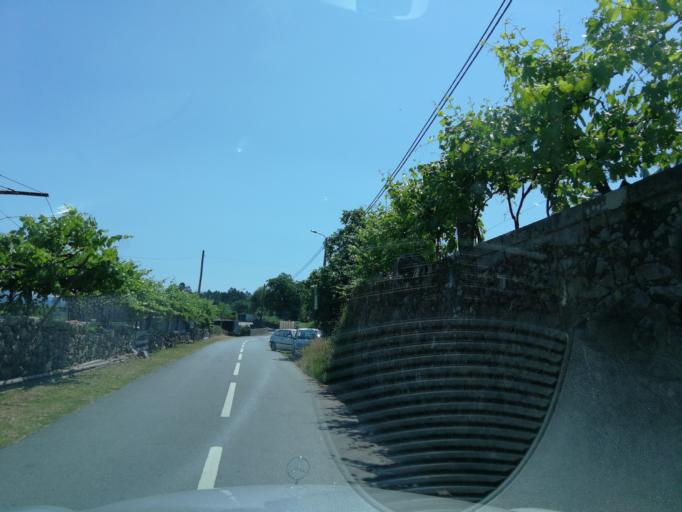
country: PT
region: Braga
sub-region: Povoa de Lanhoso
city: Povoa de Lanhoso
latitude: 41.5804
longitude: -8.3269
